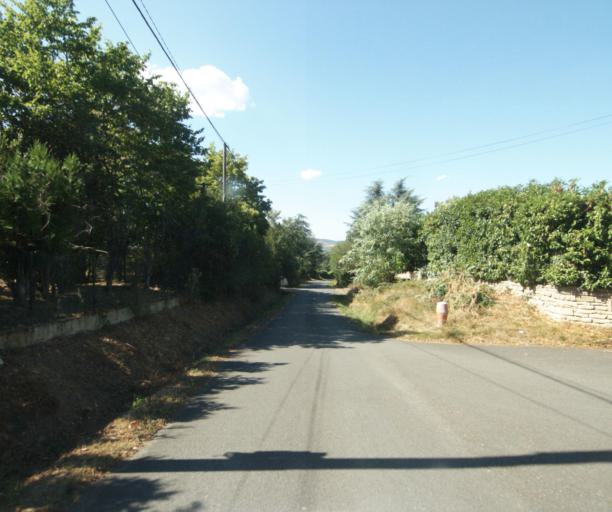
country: FR
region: Rhone-Alpes
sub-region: Departement du Rhone
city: La Tour-de-Salvagny
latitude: 45.8300
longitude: 4.6994
